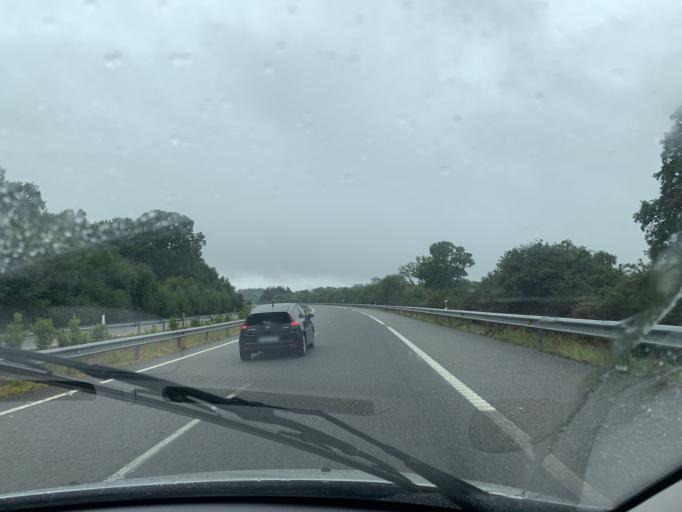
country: ES
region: Galicia
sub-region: Provincia de Lugo
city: Vilalba
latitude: 43.3298
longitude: -7.5967
